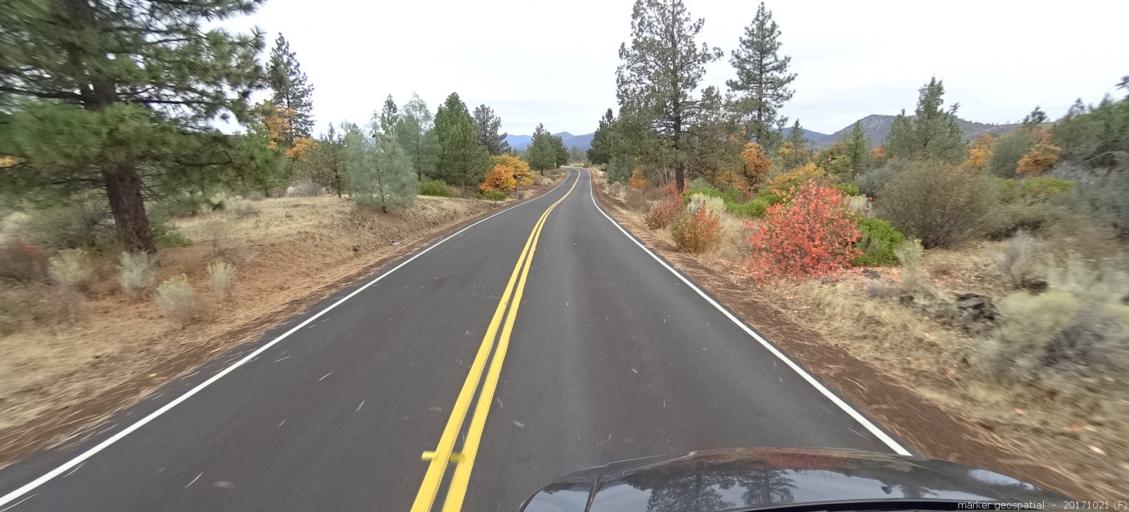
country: US
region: California
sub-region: Shasta County
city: Burney
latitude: 40.9241
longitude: -121.4590
